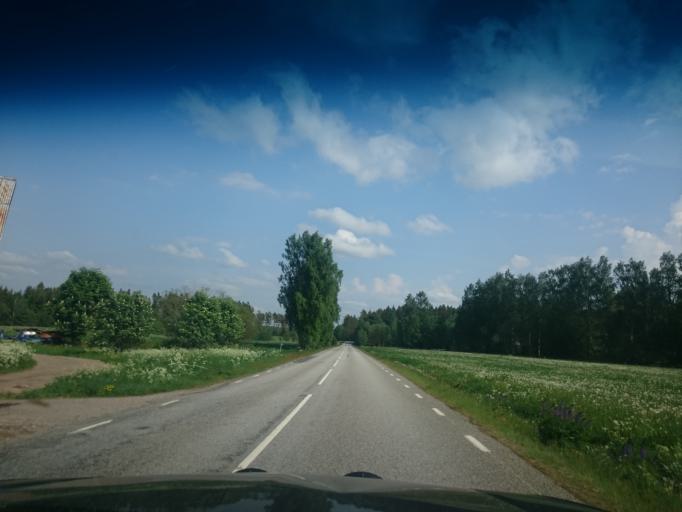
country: SE
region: Joenkoeping
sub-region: Vetlanda Kommun
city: Vetlanda
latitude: 57.3750
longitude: 15.0452
